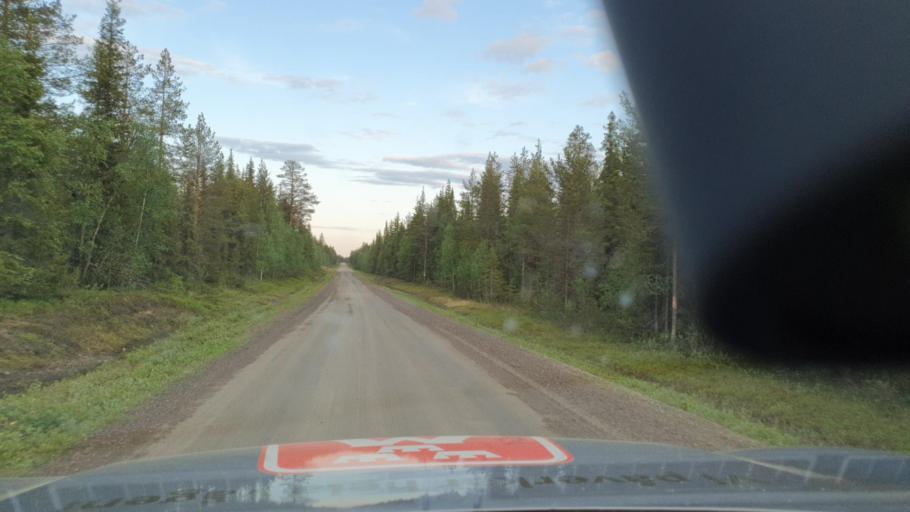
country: SE
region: Norrbotten
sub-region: Bodens Kommun
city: Boden
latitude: 66.5829
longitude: 21.3994
